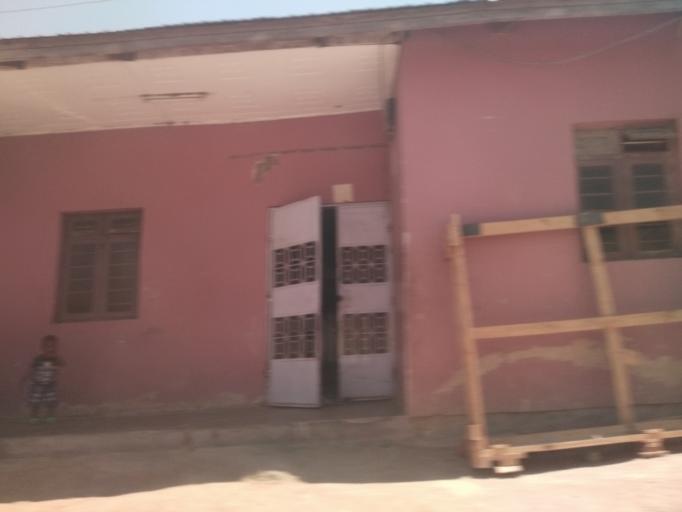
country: TZ
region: Dodoma
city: Dodoma
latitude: -6.1753
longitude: 35.7423
